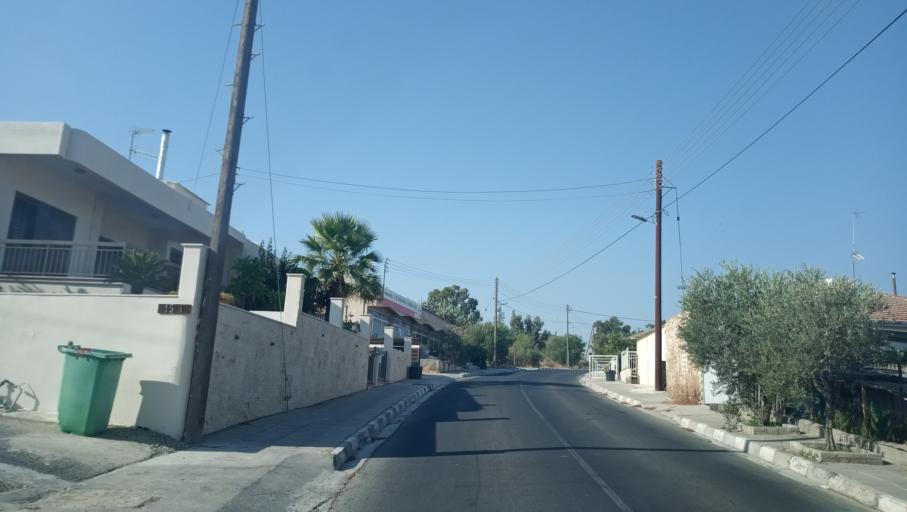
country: CY
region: Lefkosia
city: Geri
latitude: 35.1043
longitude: 33.4216
